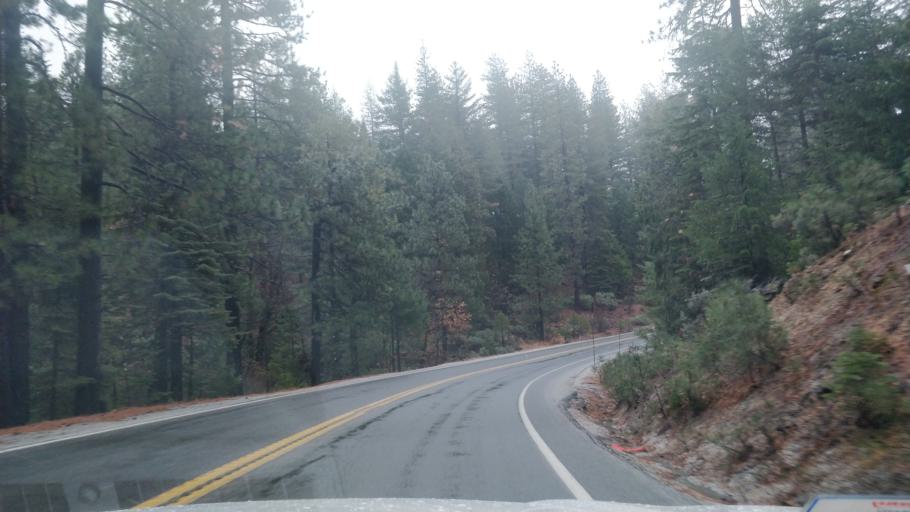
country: US
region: California
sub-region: Nevada County
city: Nevada City
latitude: 39.3220
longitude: -120.8392
